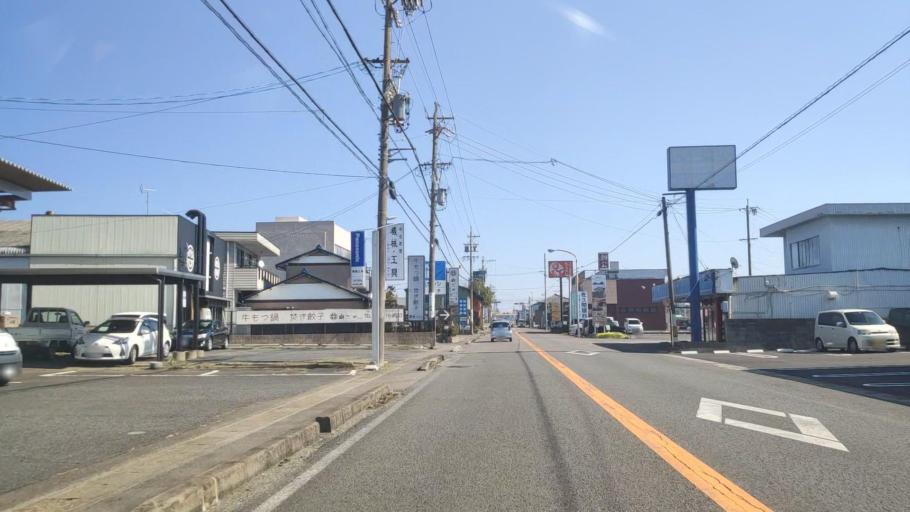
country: JP
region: Gifu
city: Kasamatsucho
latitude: 35.3925
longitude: 136.7918
